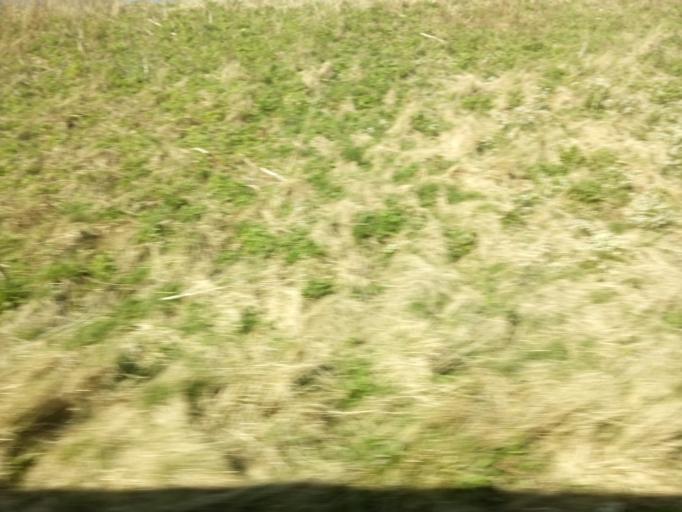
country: GB
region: England
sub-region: Northumberland
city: Berwick-Upon-Tweed
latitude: 55.8208
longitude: -2.0505
